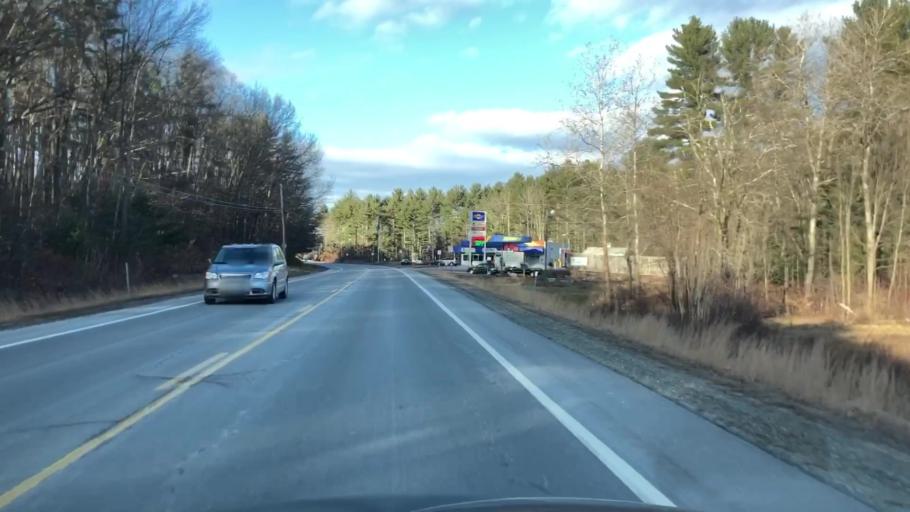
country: US
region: New Hampshire
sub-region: Hillsborough County
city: Brookline
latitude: 42.7219
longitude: -71.6625
